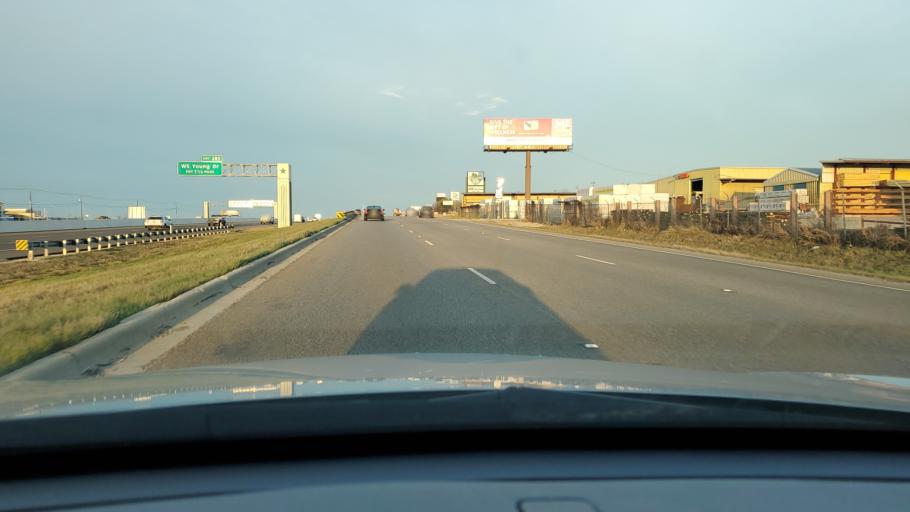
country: US
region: Texas
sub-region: Bell County
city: Harker Heights
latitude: 31.0735
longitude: -97.6784
